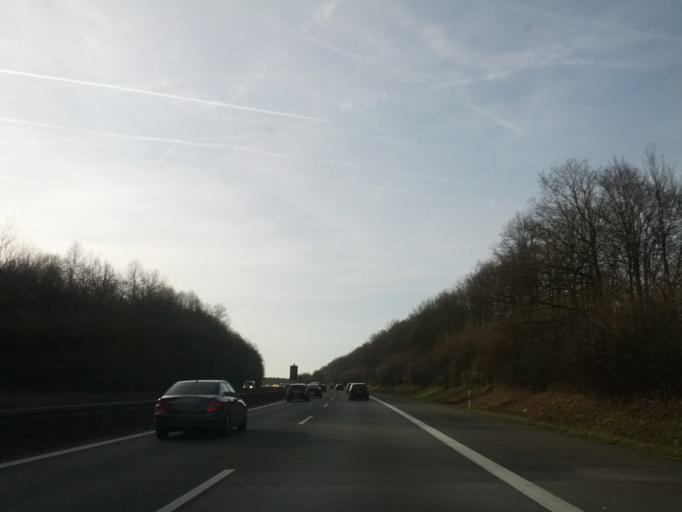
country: DE
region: Bavaria
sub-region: Regierungsbezirk Unterfranken
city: Arnstein
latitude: 49.9392
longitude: 10.0079
